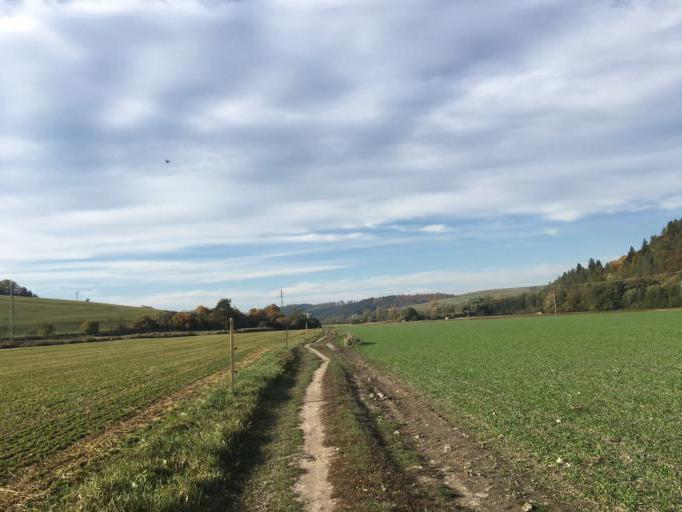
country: SK
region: Trenciansky
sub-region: Okres Povazska Bystrica
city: Povazska Bystrica
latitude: 49.0402
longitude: 18.4307
